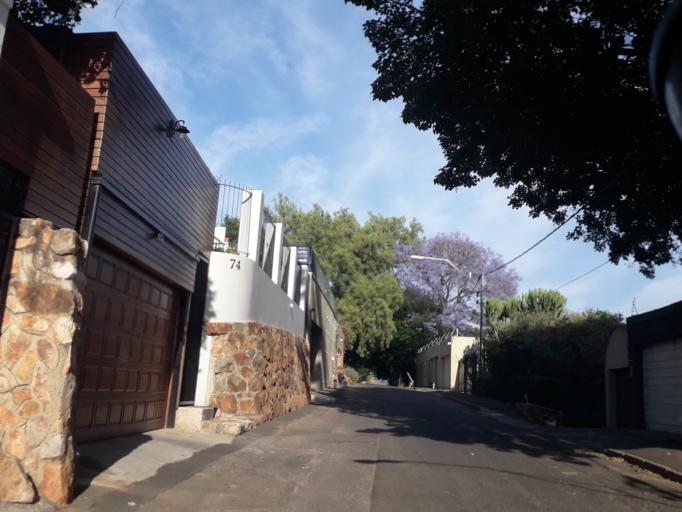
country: ZA
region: Gauteng
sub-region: City of Johannesburg Metropolitan Municipality
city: Johannesburg
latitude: -26.1745
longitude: 28.0103
